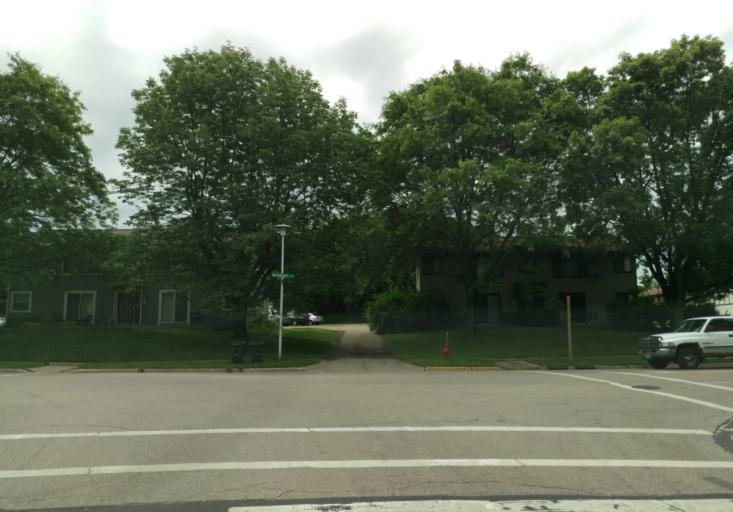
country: US
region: Wisconsin
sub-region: Dane County
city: Shorewood Hills
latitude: 43.0248
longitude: -89.4752
